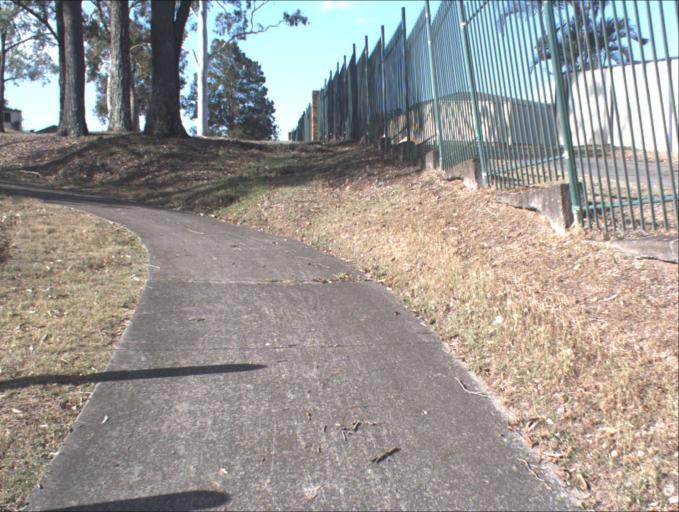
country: AU
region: Queensland
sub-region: Logan
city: Beenleigh
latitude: -27.6795
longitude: 153.2053
